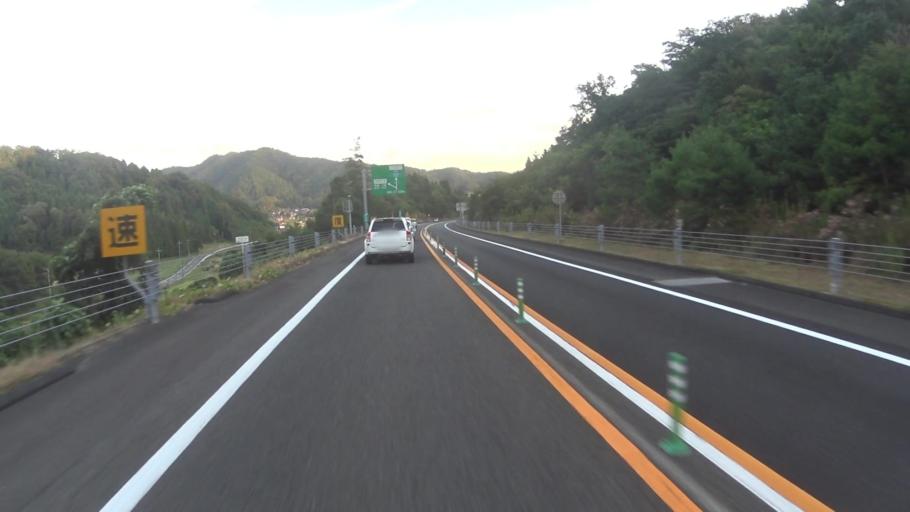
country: JP
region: Kyoto
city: Ayabe
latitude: 35.3634
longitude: 135.2881
